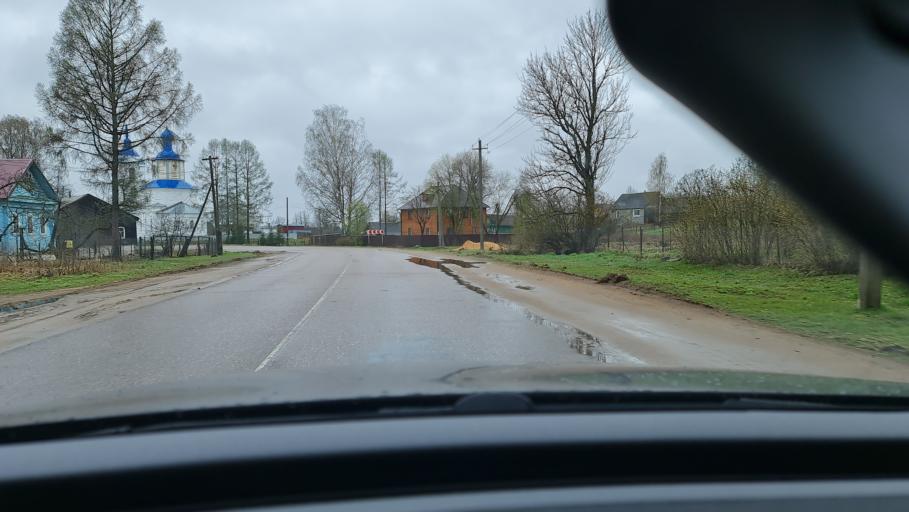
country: RU
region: Novgorod
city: Valday
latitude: 58.0367
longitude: 32.9582
